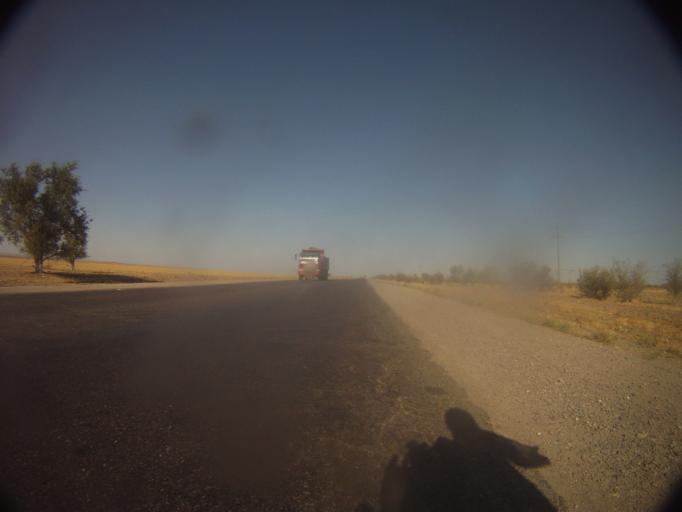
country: KZ
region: Zhambyl
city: Sarykemer
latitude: 42.9744
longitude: 71.5679
